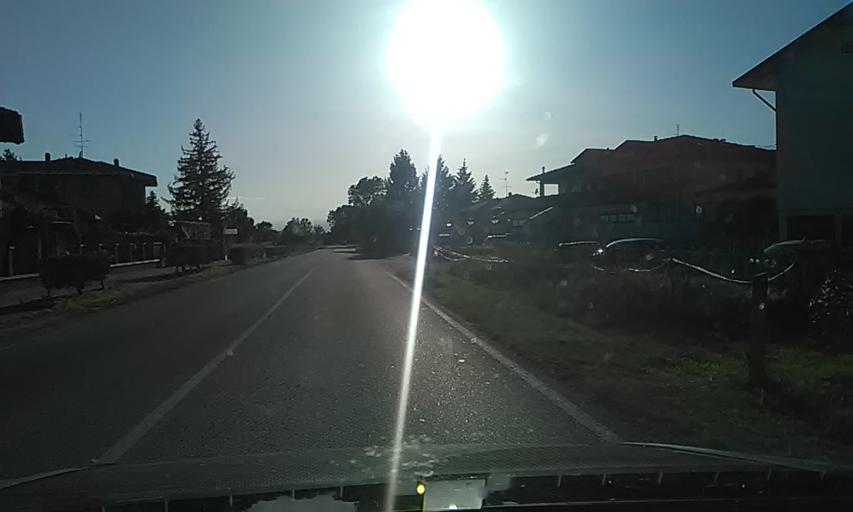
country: IT
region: Piedmont
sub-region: Provincia di Novara
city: Oleggio
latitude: 45.5947
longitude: 8.6207
